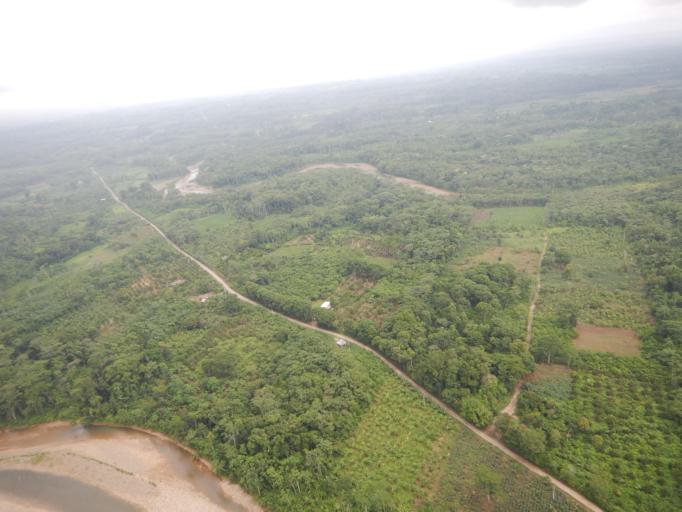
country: BO
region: Cochabamba
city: Chimore
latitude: -17.2399
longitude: -64.6463
